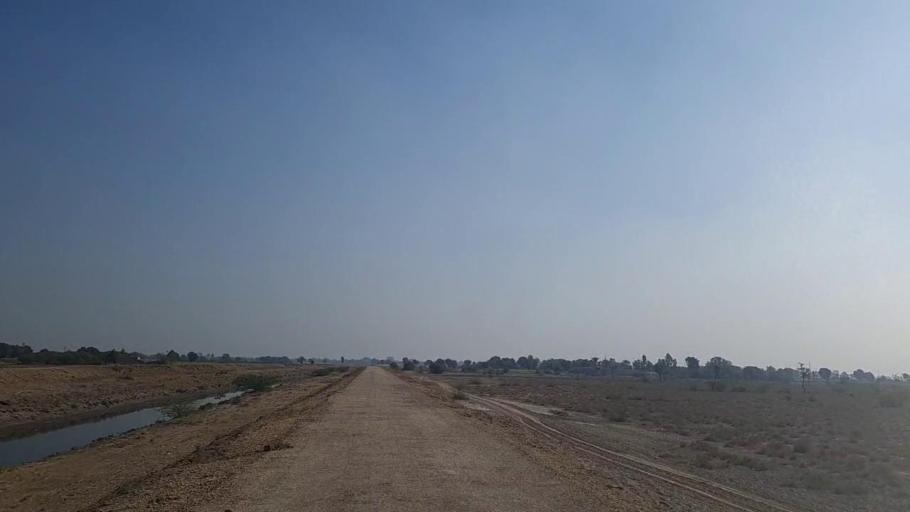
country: PK
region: Sindh
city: Shahpur Chakar
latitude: 26.1861
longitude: 68.5608
